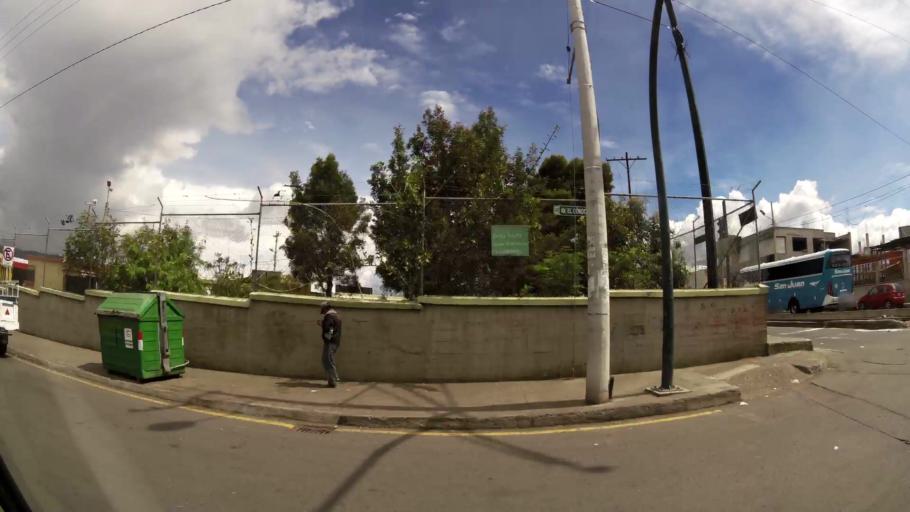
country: EC
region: Tungurahua
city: Ambato
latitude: -1.2700
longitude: -78.6168
